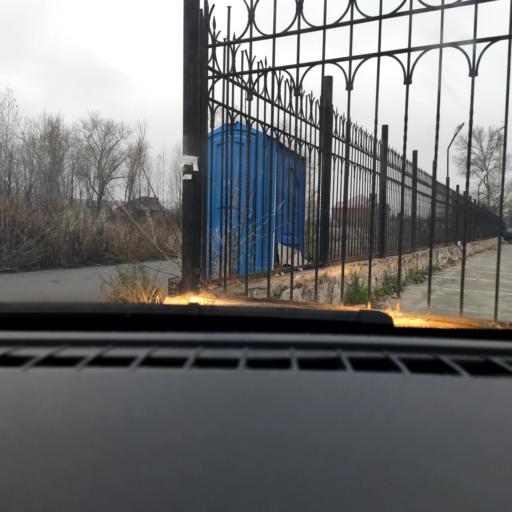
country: RU
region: Voronezj
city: Voronezh
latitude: 51.6290
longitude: 39.1642
